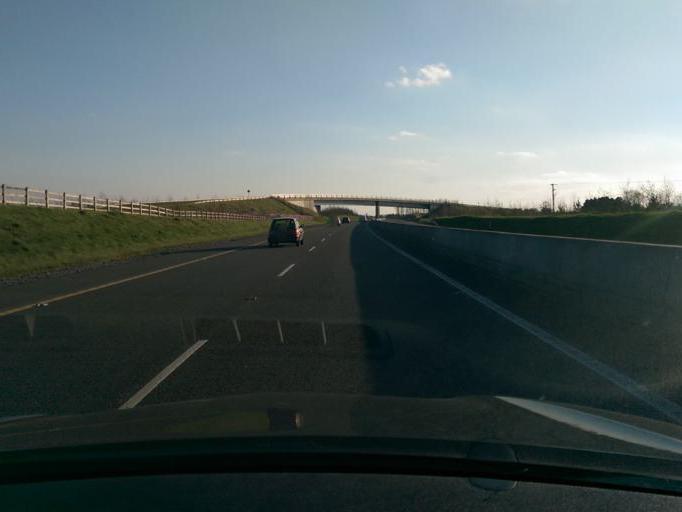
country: IE
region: Leinster
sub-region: Laois
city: Mountrath
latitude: 52.9707
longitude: -7.4350
